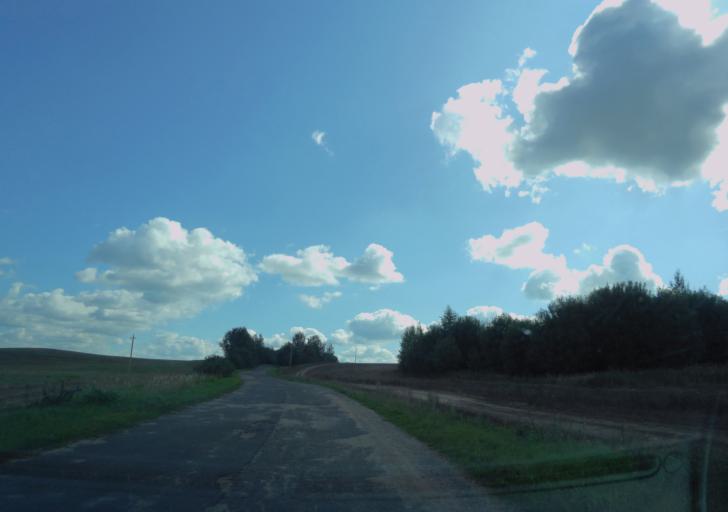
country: BY
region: Minsk
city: Zyembin
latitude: 54.4085
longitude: 28.3910
